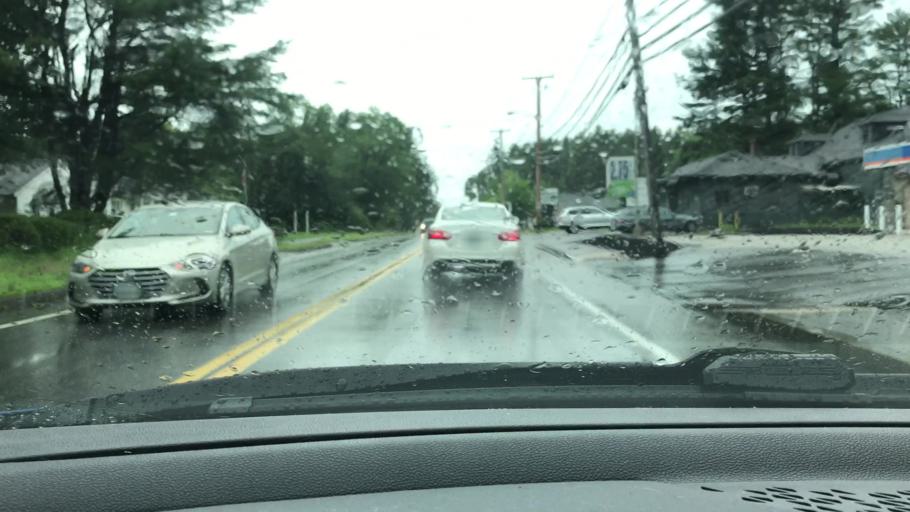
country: US
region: New Hampshire
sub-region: Merrimack County
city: East Concord
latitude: 43.2534
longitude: -71.5757
